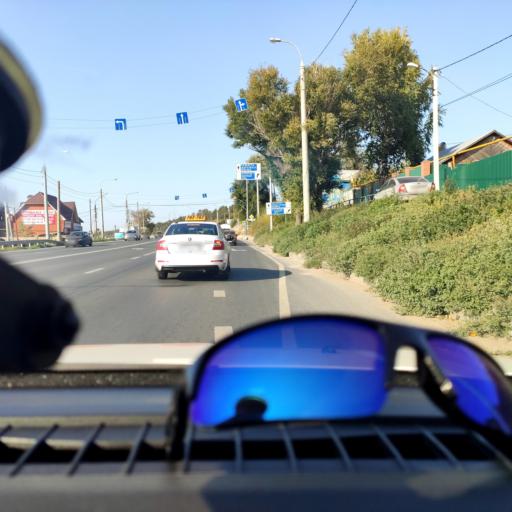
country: RU
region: Samara
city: Volzhskiy
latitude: 53.4302
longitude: 50.1188
